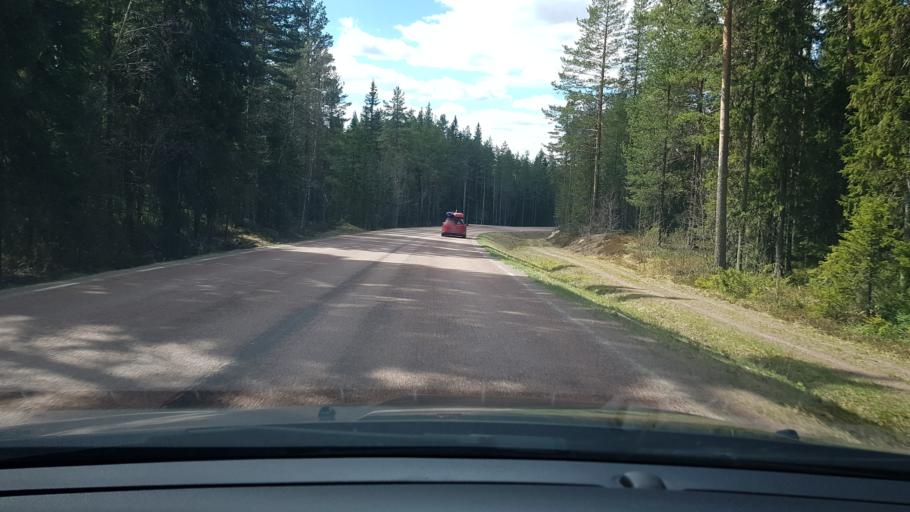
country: SE
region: Dalarna
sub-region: Alvdalens Kommun
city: AElvdalen
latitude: 61.0839
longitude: 13.7344
